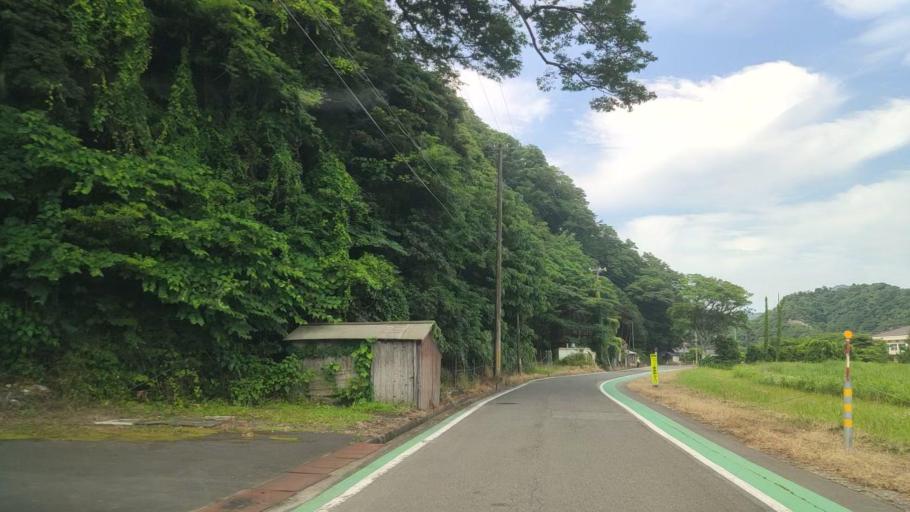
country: JP
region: Hyogo
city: Toyooka
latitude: 35.6421
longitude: 134.8422
